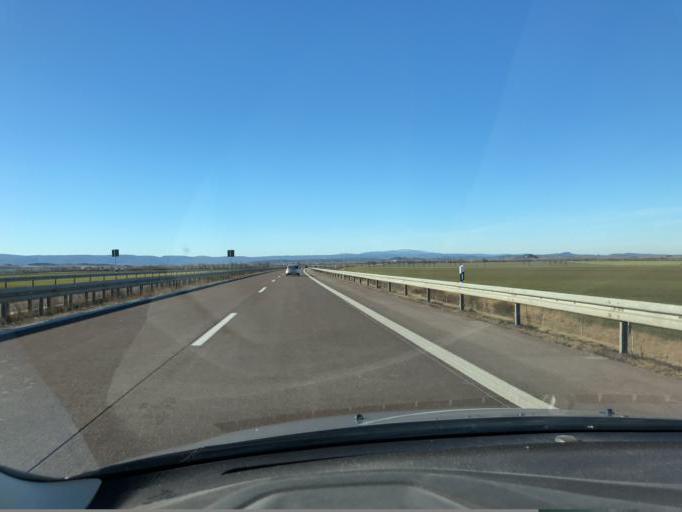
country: DE
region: Saxony-Anhalt
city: Gatersleben
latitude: 51.8015
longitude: 11.2441
